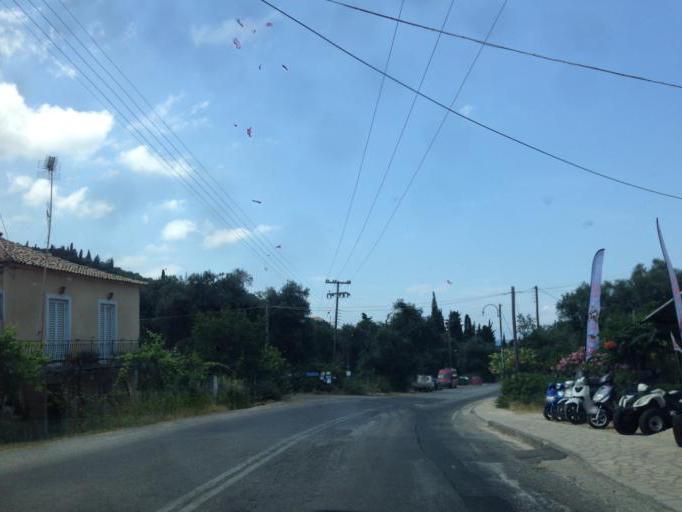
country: GR
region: Ionian Islands
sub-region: Nomos Kerkyras
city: Acharavi
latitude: 39.7845
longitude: 19.9217
